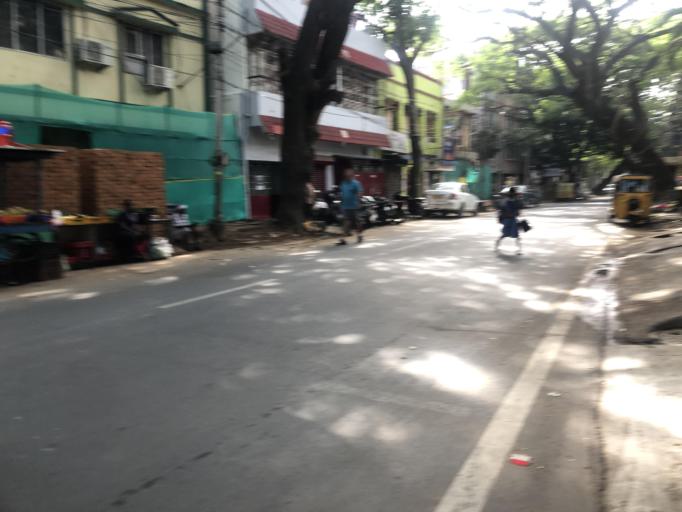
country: IN
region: Tamil Nadu
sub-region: Chennai
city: Gandhi Nagar
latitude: 13.0333
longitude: 80.2583
